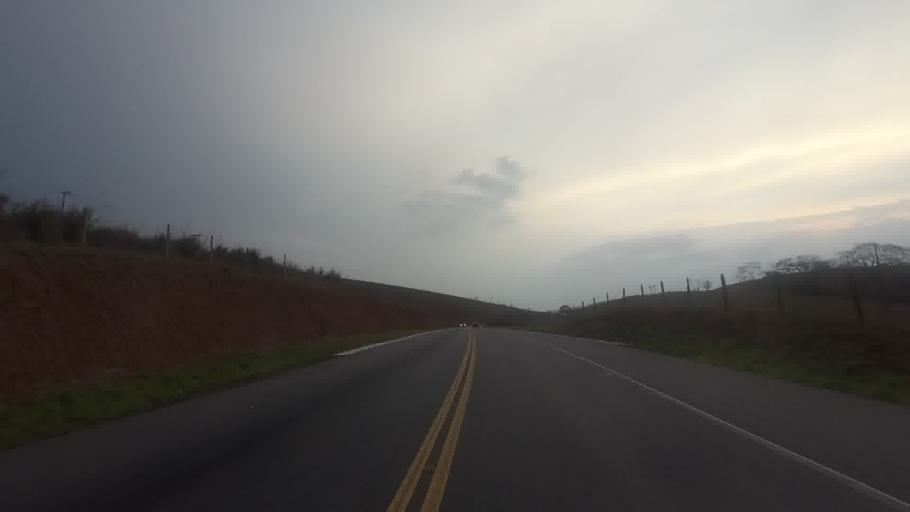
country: BR
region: Rio de Janeiro
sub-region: Carmo
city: Carmo
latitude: -21.8054
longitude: -42.5768
